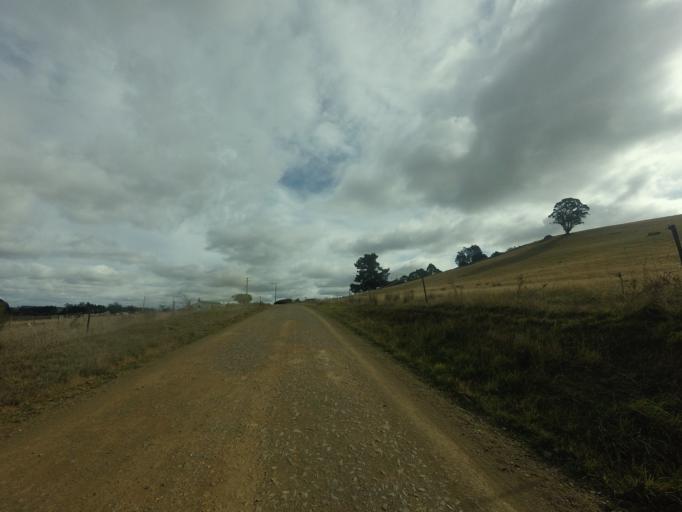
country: AU
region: Tasmania
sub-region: Sorell
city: Sorell
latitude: -42.4296
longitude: 147.4641
